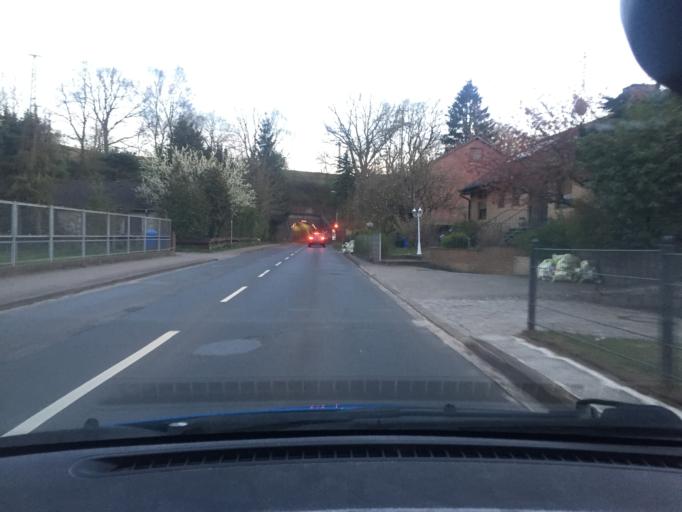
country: DE
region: Lower Saxony
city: Buchholz in der Nordheide
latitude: 53.3237
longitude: 9.8579
